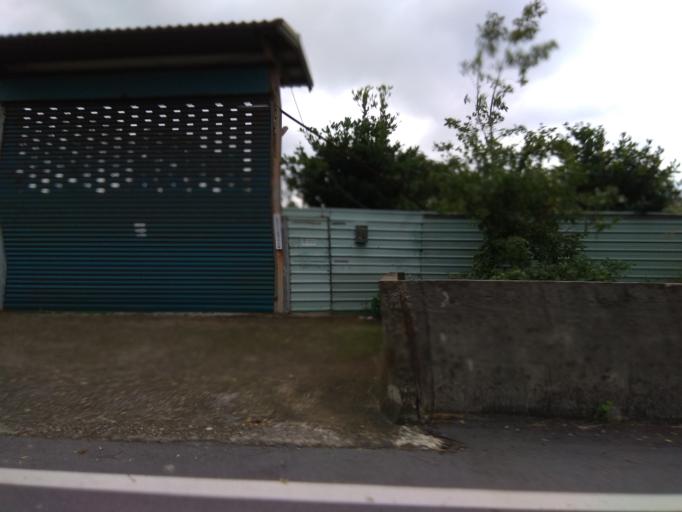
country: TW
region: Taiwan
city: Taoyuan City
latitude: 25.0440
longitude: 121.2183
